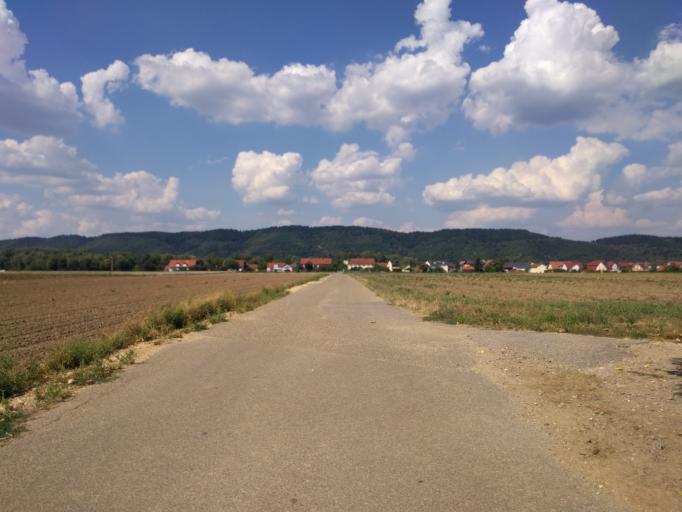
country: DE
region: Bavaria
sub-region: Upper Palatinate
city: Mintraching
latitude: 49.0036
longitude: 12.2715
